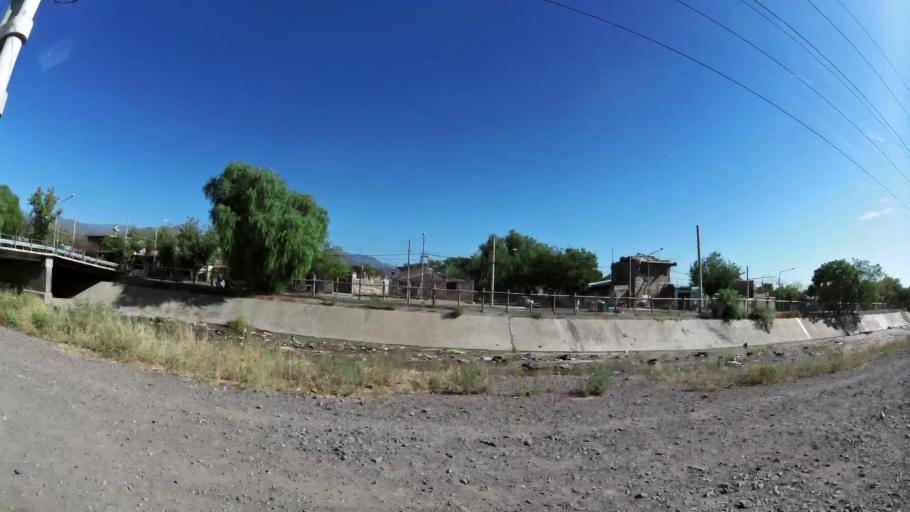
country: AR
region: Mendoza
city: Las Heras
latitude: -32.8709
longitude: -68.8635
